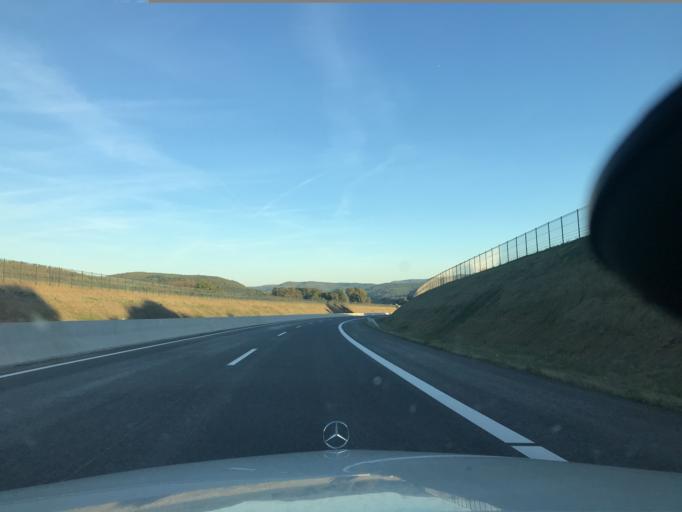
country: DE
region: Hesse
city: Waldkappel
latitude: 51.1554
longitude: 9.8888
